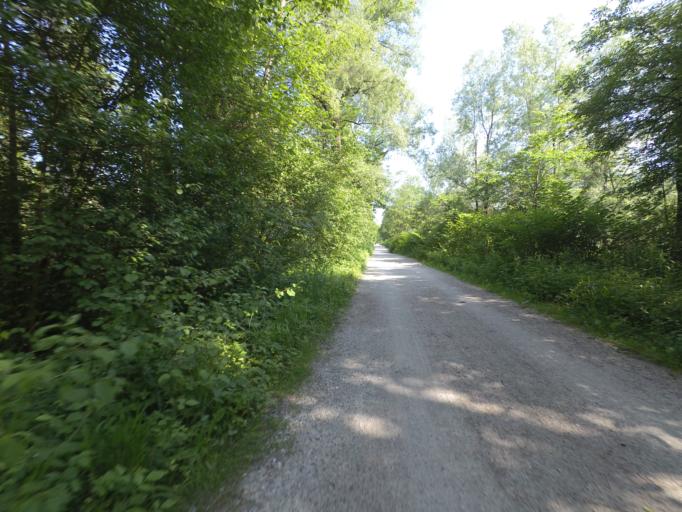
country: AT
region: Salzburg
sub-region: Politischer Bezirk Salzburg-Umgebung
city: Elsbethen
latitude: 47.7575
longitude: 13.0774
